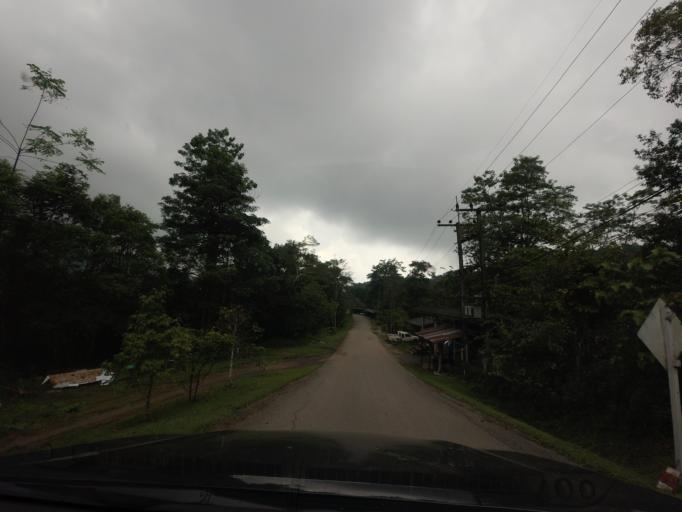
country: TH
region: Nan
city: Bo Kluea
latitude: 19.2017
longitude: 101.0814
